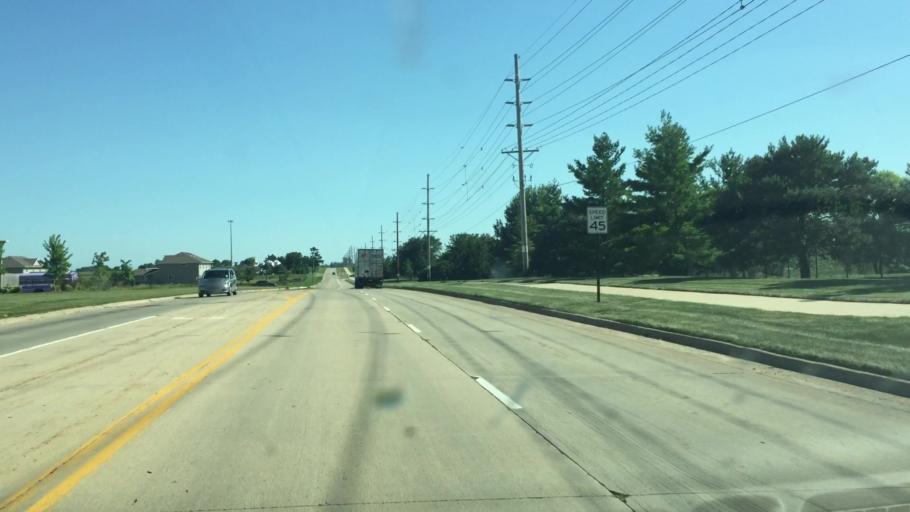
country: US
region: Iowa
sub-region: Linn County
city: Ely
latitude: 41.9179
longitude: -91.6373
